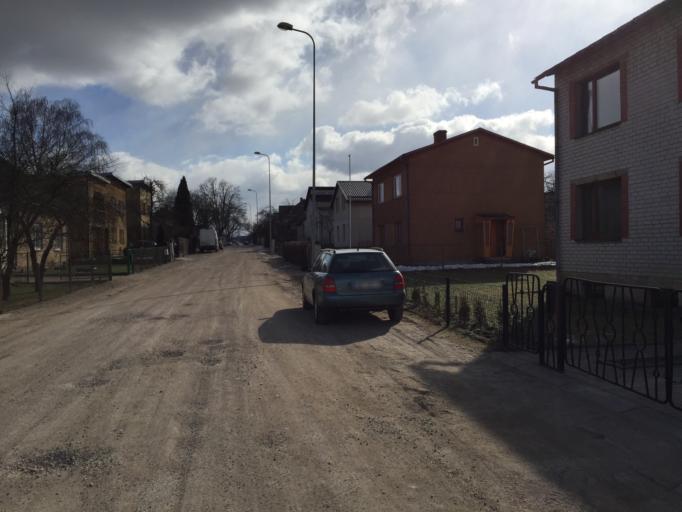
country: LV
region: Valmieras Rajons
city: Valmiera
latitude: 57.5480
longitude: 25.4285
